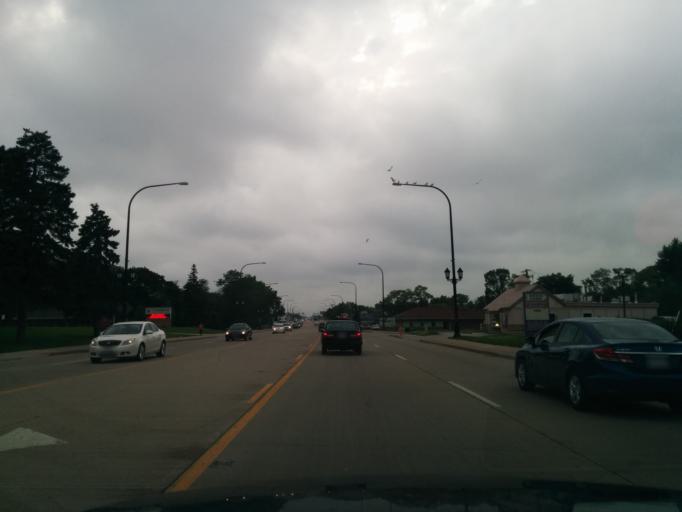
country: US
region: Illinois
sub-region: DuPage County
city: Addison
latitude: 41.9356
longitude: -87.9966
